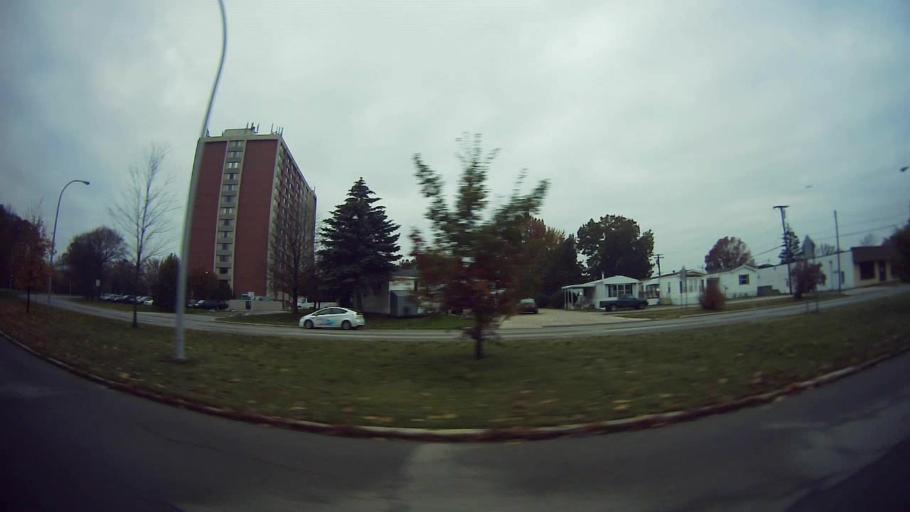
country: US
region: Michigan
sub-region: Wayne County
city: Dearborn Heights
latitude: 42.3412
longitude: -83.2518
